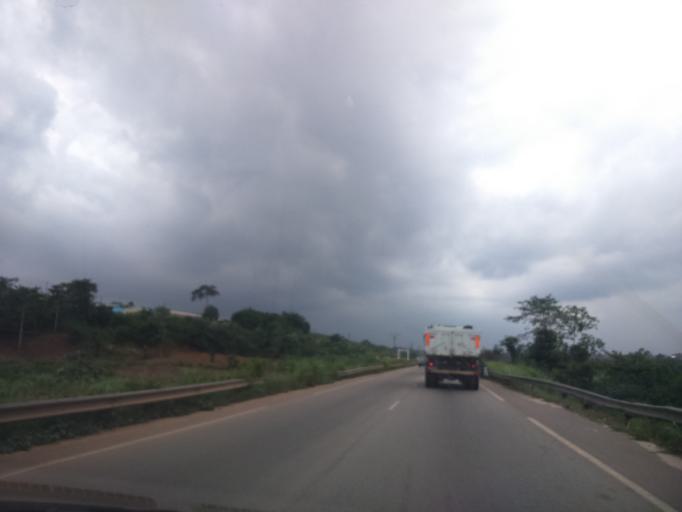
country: CI
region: Lagunes
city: Anyama
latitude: 5.5067
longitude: -4.0629
